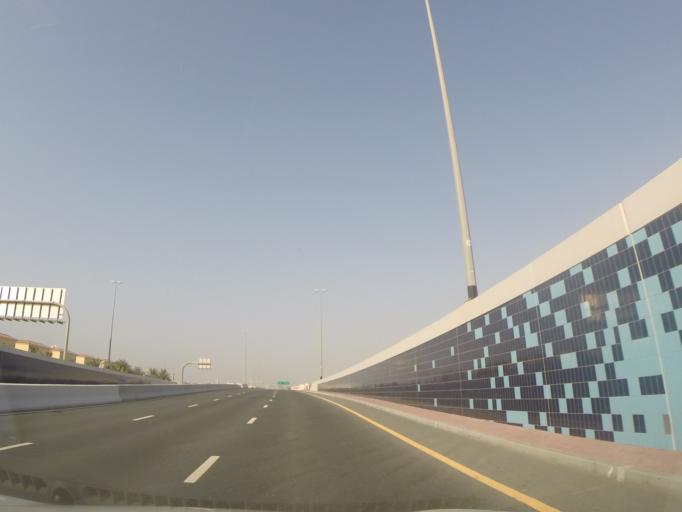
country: AE
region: Dubai
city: Dubai
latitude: 25.0479
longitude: 55.1667
